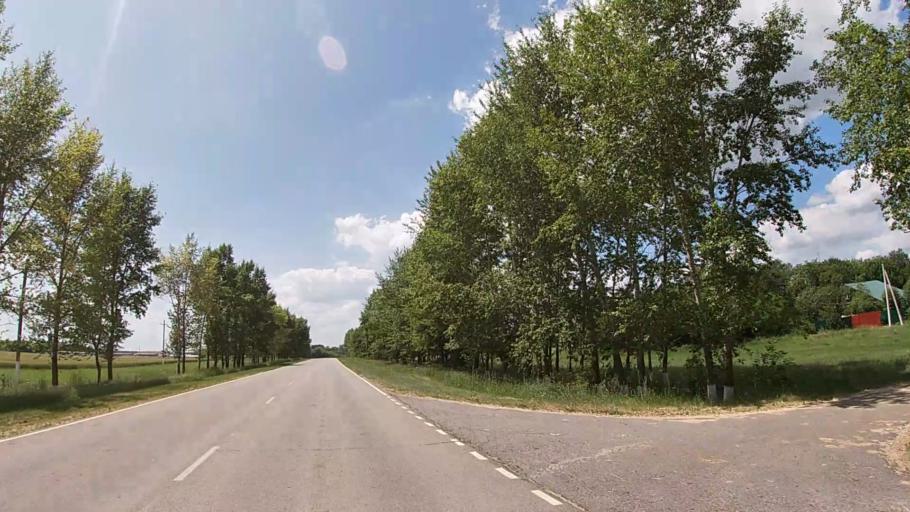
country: RU
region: Belgorod
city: Grayvoron
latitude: 50.4384
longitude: 35.6086
